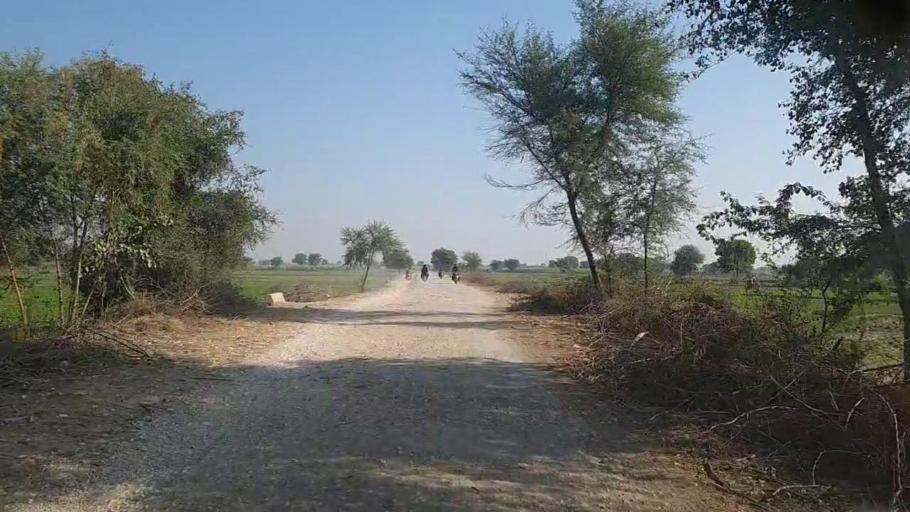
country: PK
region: Sindh
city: Darya Khan Marri
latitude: 26.6715
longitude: 68.3260
